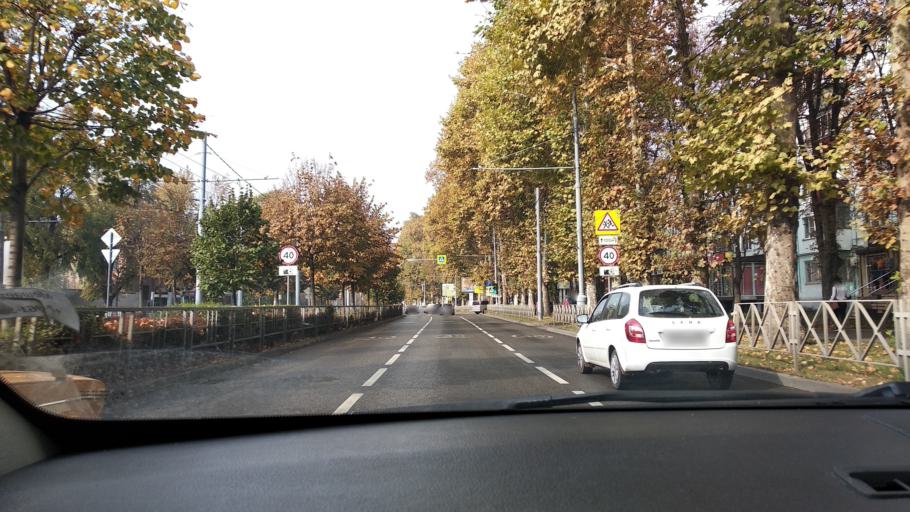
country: RU
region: Krasnodarskiy
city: Krasnodar
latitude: 45.0212
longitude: 39.0208
